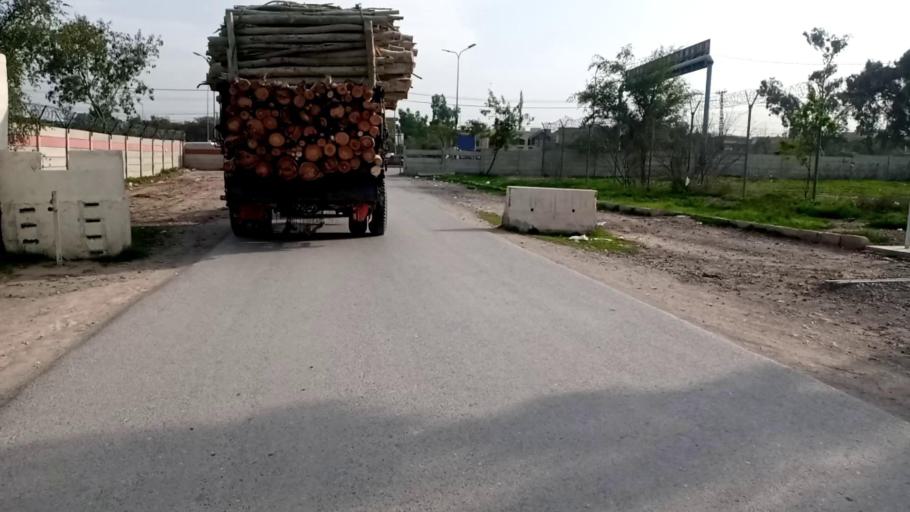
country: PK
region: Khyber Pakhtunkhwa
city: Peshawar
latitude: 33.9976
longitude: 71.4525
